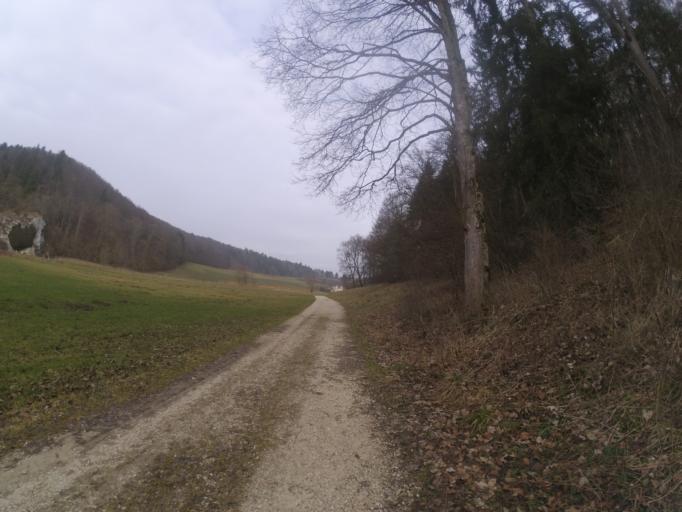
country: DE
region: Baden-Wuerttemberg
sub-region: Tuebingen Region
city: Hayingen
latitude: 48.2989
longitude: 9.4948
